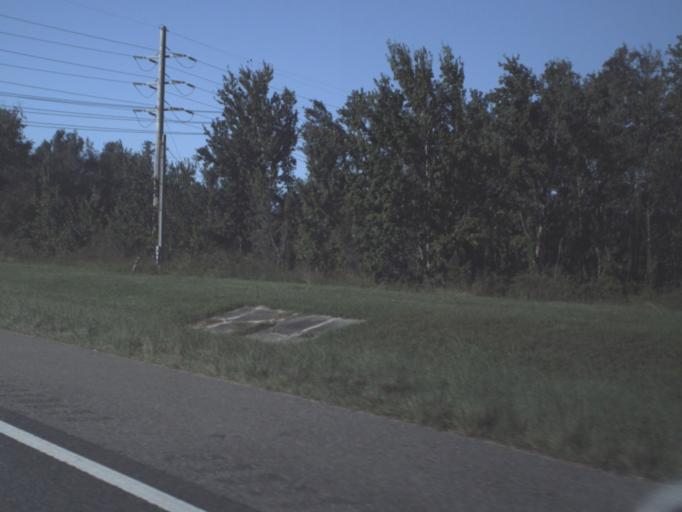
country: US
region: Florida
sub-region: Seminole County
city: Oviedo
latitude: 28.6415
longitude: -81.2410
